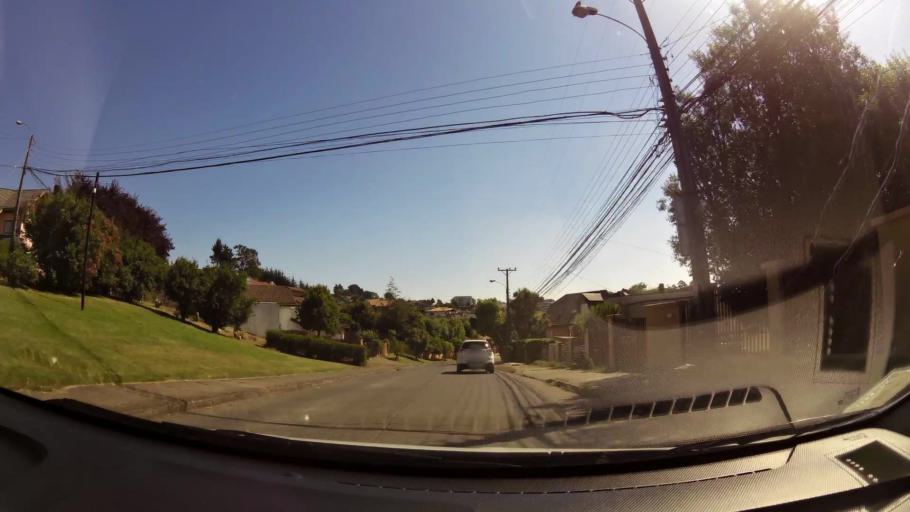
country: CL
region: Biobio
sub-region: Provincia de Concepcion
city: Concepcion
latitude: -36.7909
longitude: -73.0541
